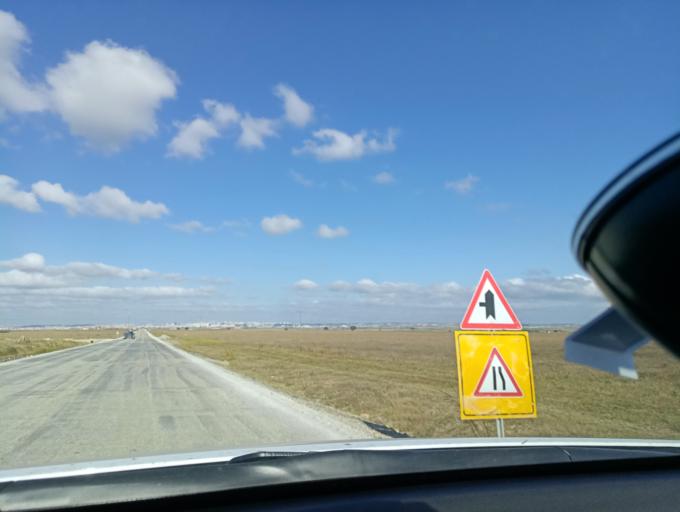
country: TR
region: Tekirdag
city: Corlu
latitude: 41.0660
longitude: 27.8338
